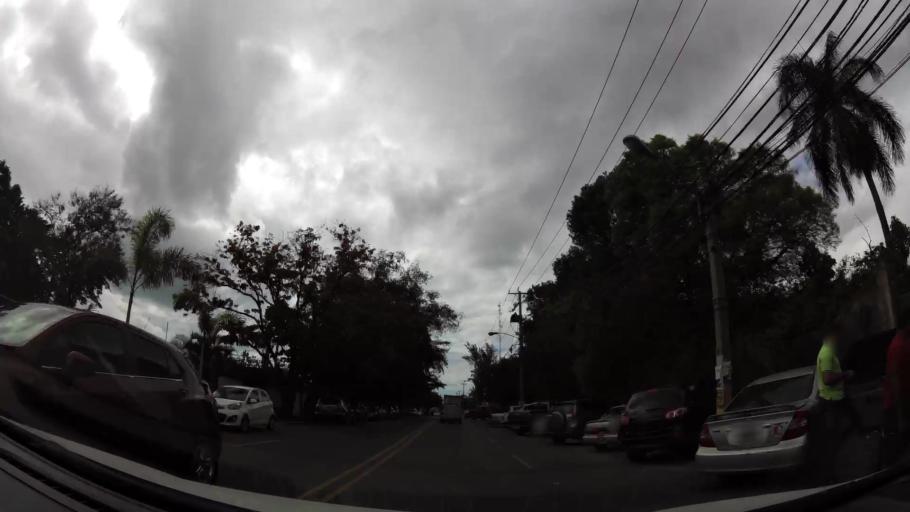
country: DO
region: Nacional
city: Bella Vista
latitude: 18.4729
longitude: -69.9576
